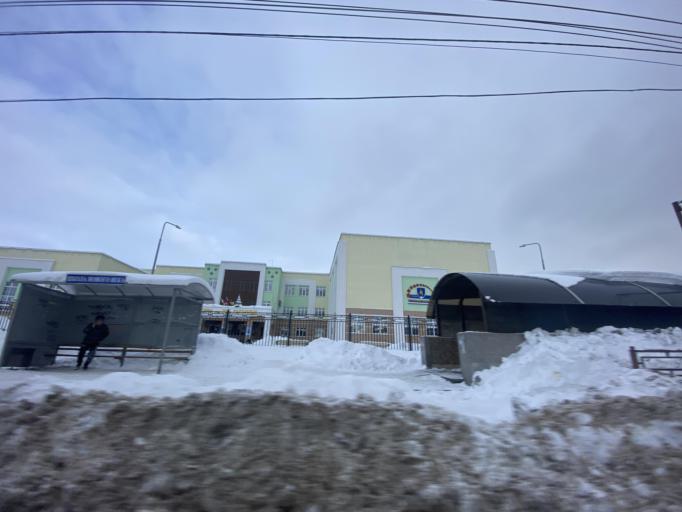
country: RU
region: Saratov
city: Engel's
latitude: 51.4977
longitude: 46.0895
